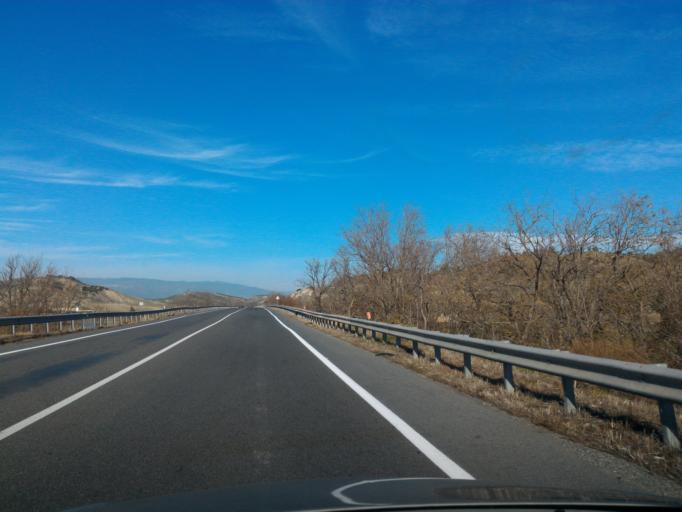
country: IT
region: Calabria
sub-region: Provincia di Crotone
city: Le Castella
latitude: 38.9431
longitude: 16.9556
